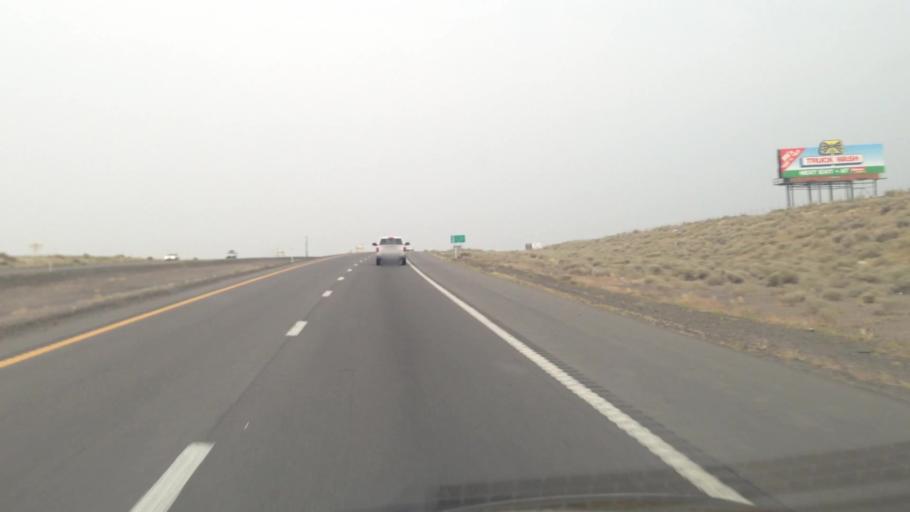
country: US
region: Nevada
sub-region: Lyon County
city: Fernley
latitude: 39.6180
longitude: -119.2820
